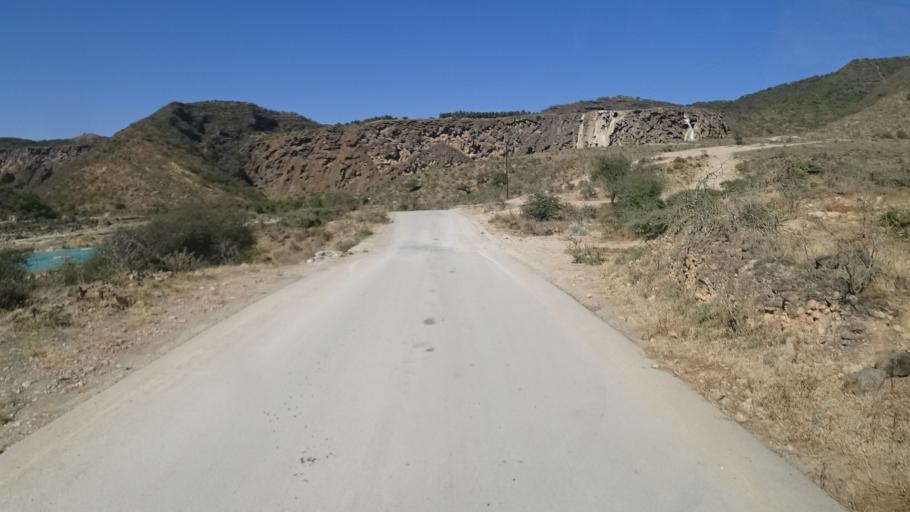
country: OM
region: Zufar
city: Salalah
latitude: 17.0713
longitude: 54.4319
